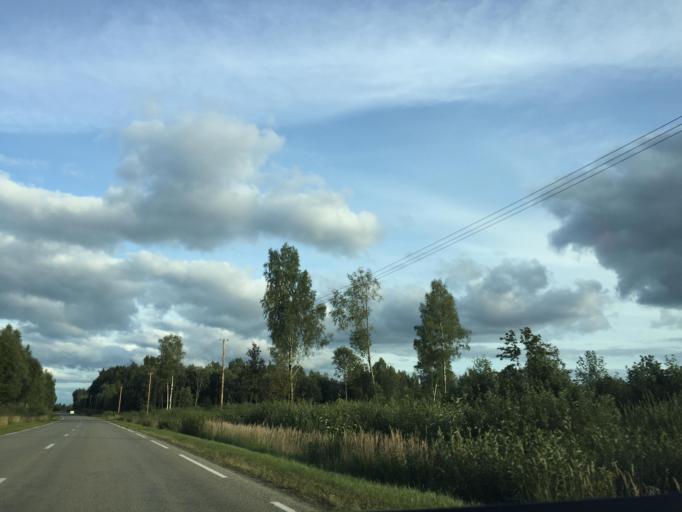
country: LV
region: Nereta
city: Nereta
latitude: 56.2893
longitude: 25.1264
